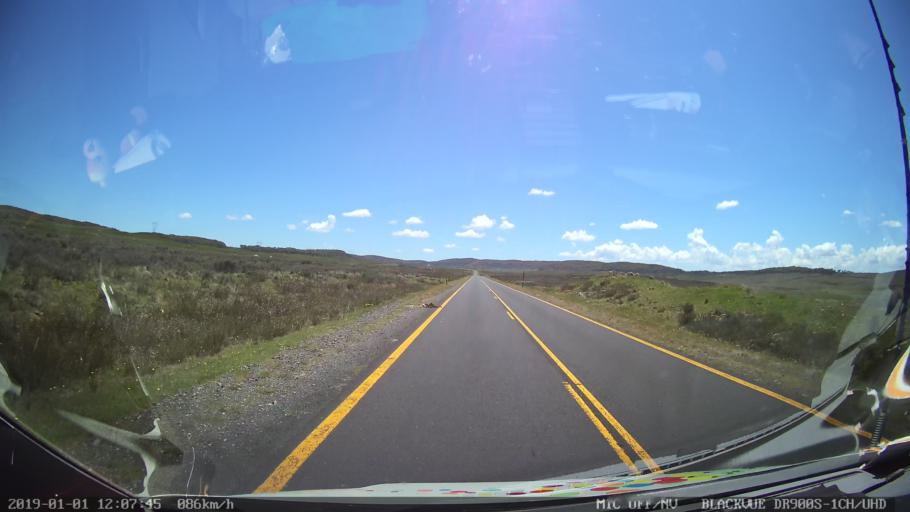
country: AU
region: New South Wales
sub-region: Tumut Shire
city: Tumut
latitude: -35.8291
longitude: 148.4912
